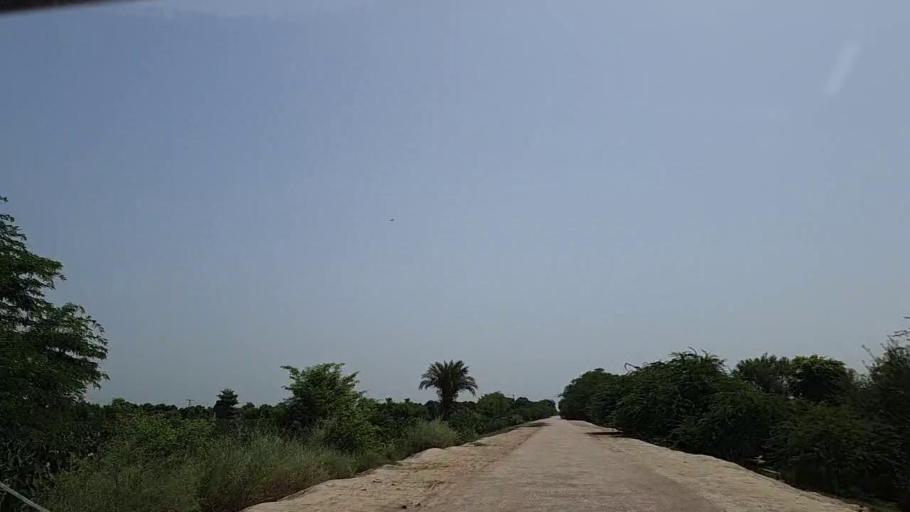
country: PK
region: Sindh
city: Kandiaro
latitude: 27.0411
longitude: 68.1292
